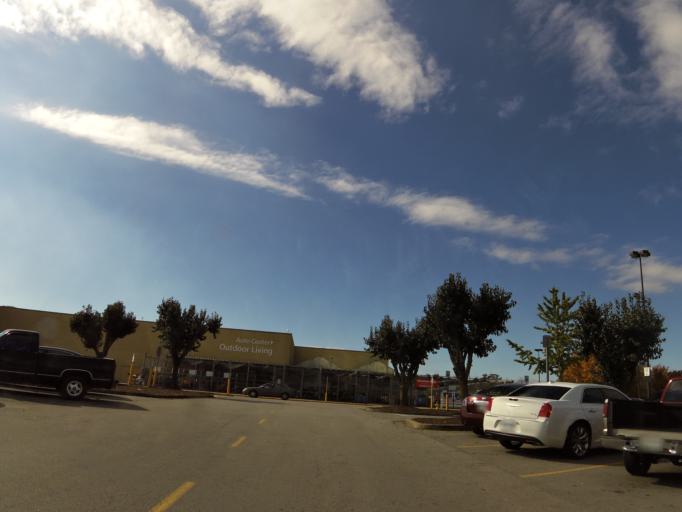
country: US
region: Tennessee
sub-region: Blount County
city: Alcoa
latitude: 35.7722
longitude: -83.9906
